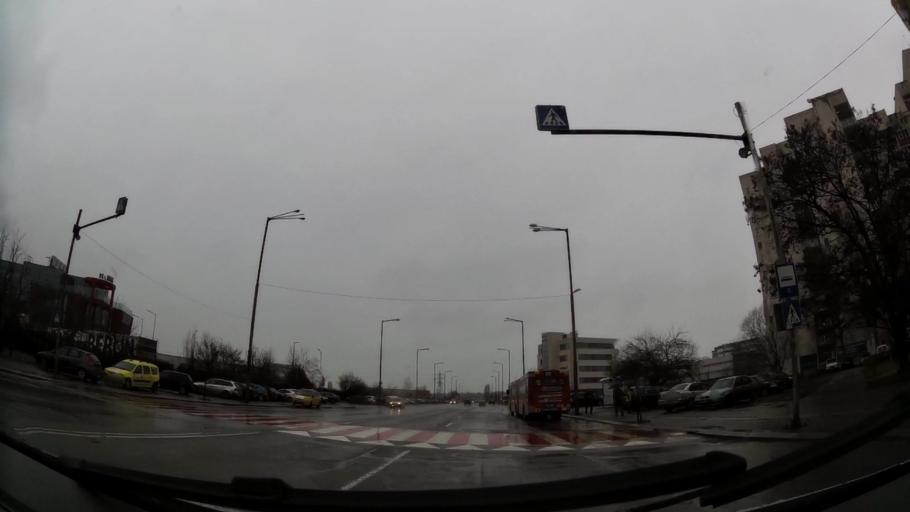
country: BG
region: Sofia-Capital
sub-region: Stolichna Obshtina
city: Sofia
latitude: 42.6492
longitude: 23.4089
